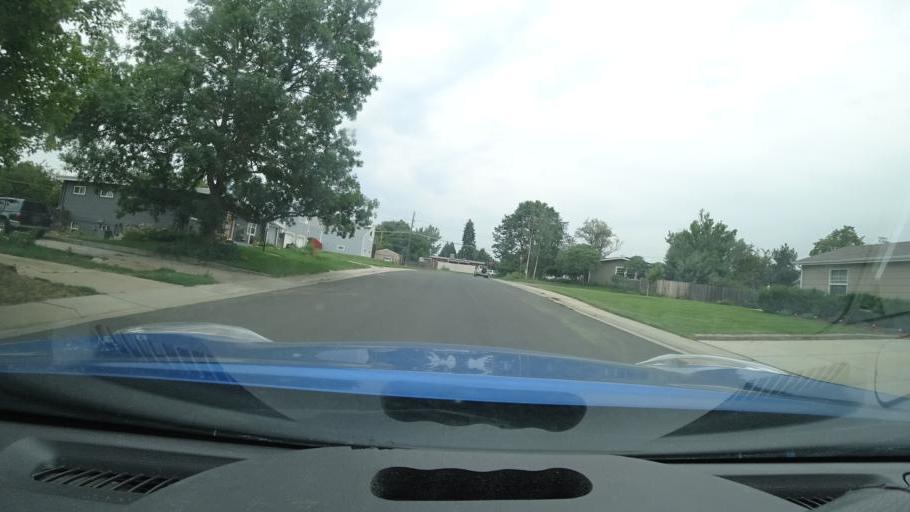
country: US
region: Colorado
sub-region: Arapahoe County
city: Glendale
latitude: 39.6902
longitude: -104.9161
